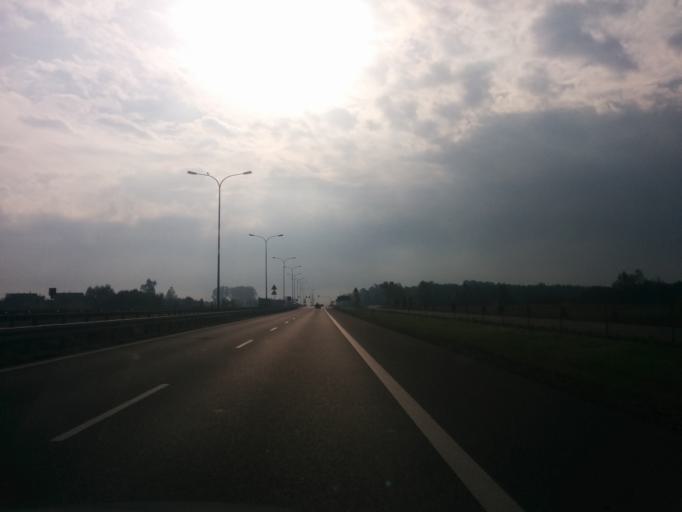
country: PL
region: Masovian Voivodeship
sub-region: Powiat radomski
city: Jedlinsk
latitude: 51.5332
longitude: 21.0784
